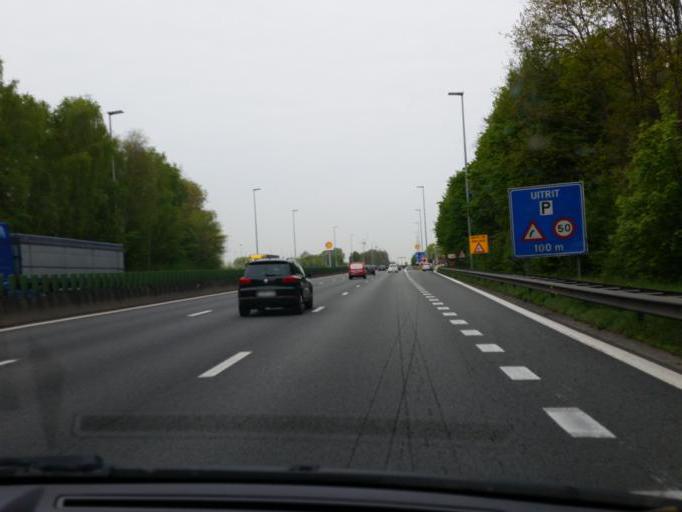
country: BE
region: Flanders
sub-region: Provincie Oost-Vlaanderen
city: Sint-Lievens-Houtem
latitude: 50.9683
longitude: 3.8471
